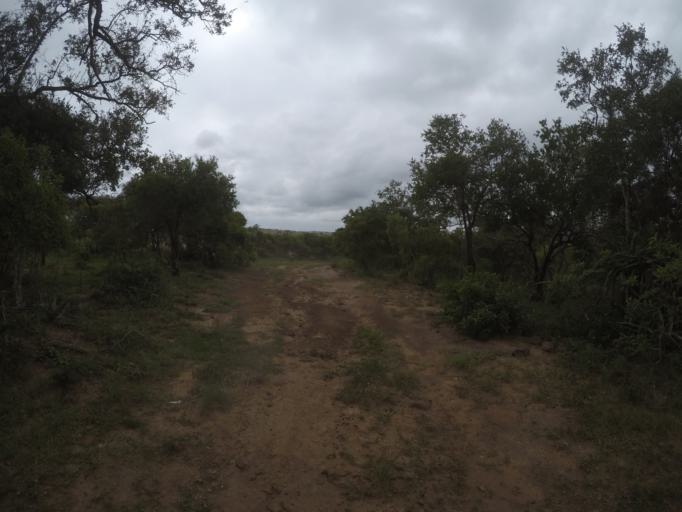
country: ZA
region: KwaZulu-Natal
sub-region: uThungulu District Municipality
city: Empangeni
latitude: -28.5925
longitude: 31.8464
